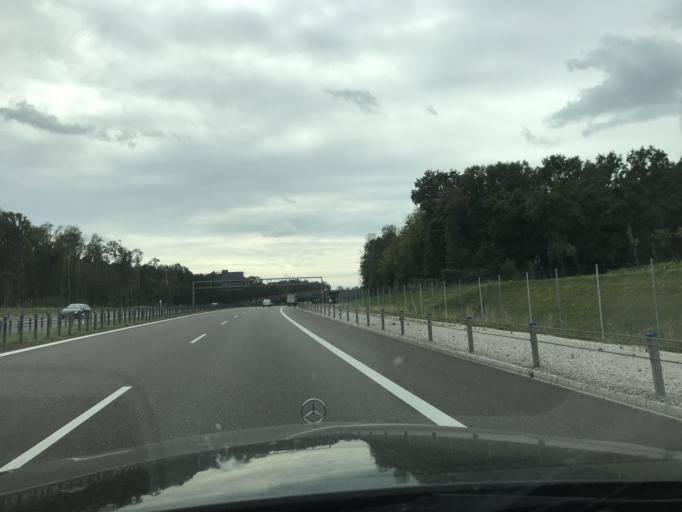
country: PL
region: Lublin Voivodeship
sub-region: Powiat lubelski
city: Kozubszczyzna
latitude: 51.2046
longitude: 22.4442
